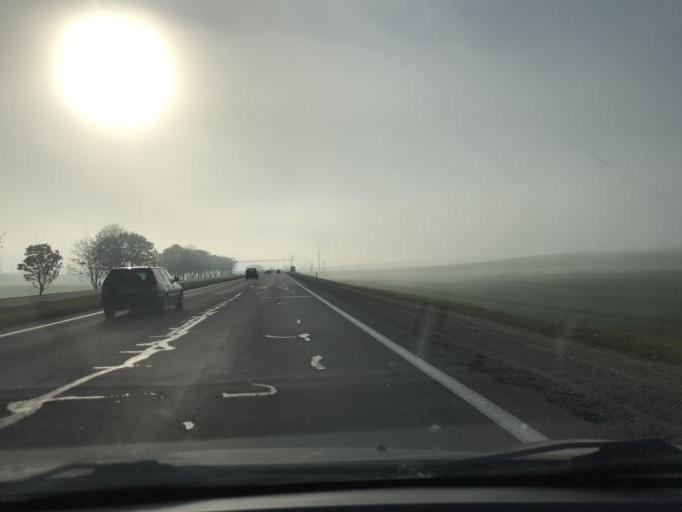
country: BY
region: Minsk
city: Luhavaya Slabada
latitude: 53.7414
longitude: 27.8418
